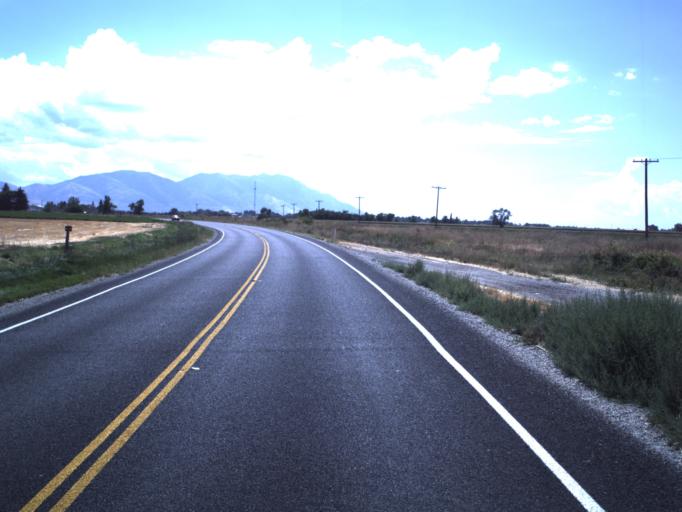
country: US
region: Utah
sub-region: Box Elder County
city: Elwood
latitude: 41.6519
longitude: -112.1397
